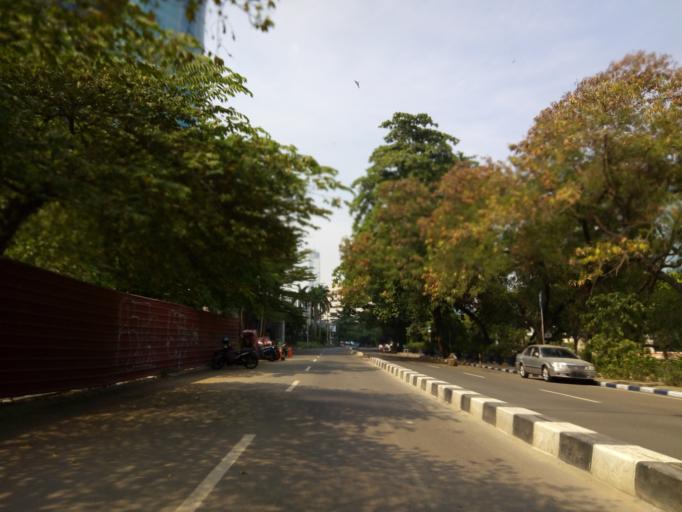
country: ID
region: Jakarta Raya
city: Jakarta
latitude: -6.2091
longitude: 106.8308
